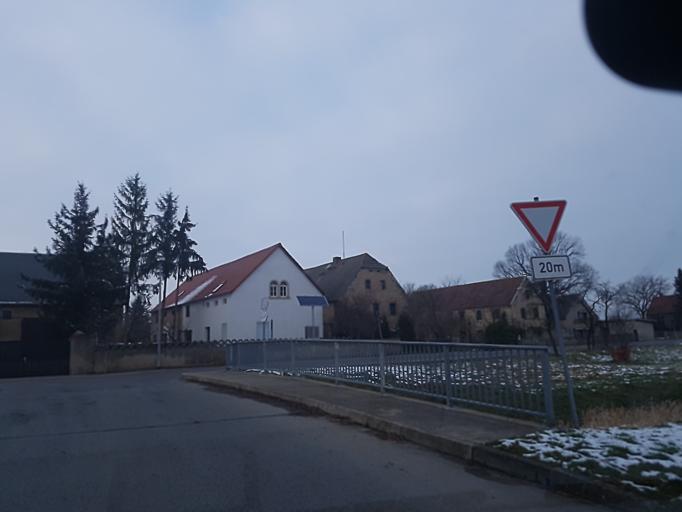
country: DE
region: Saxony
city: Cavertitz
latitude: 51.3864
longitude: 13.1566
